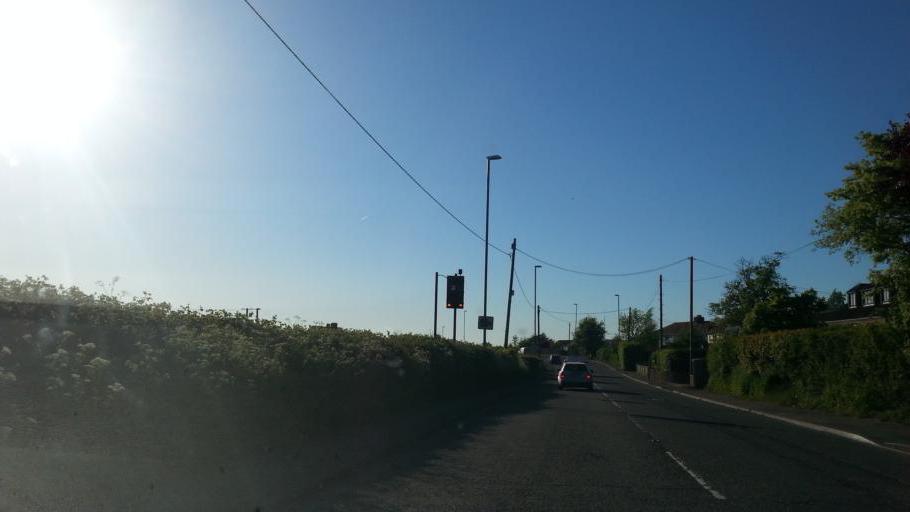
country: GB
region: England
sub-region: Bath and North East Somerset
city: Whitchurch
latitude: 51.4032
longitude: -2.5544
